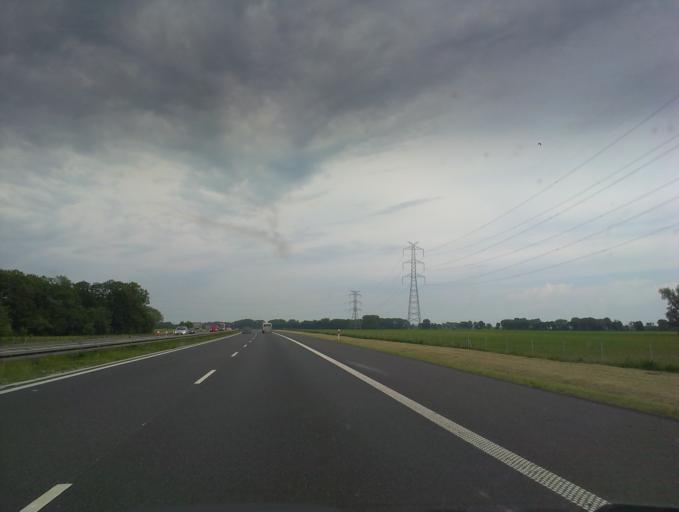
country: PL
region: Opole Voivodeship
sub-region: Powiat brzeski
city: Grodkow
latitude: 50.7744
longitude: 17.3653
